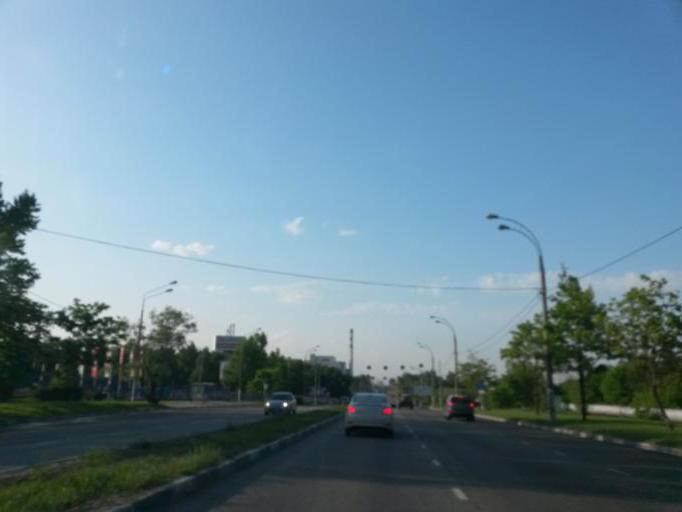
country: RU
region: Moskovskaya
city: Biryulevo Zapadnoye
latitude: 55.5919
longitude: 37.6355
